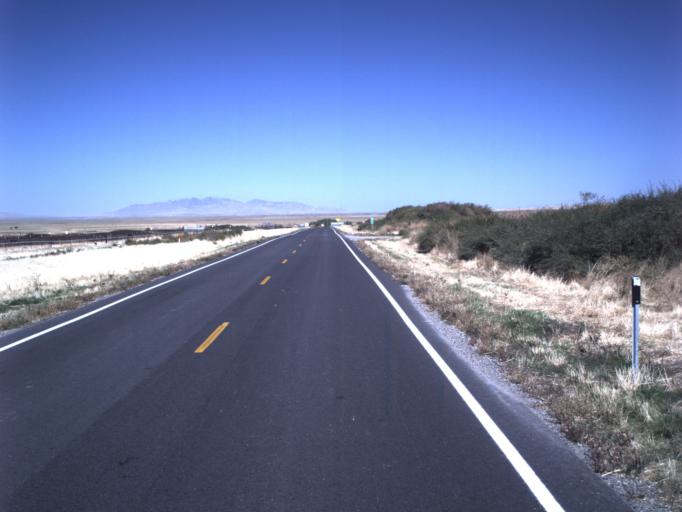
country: US
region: Utah
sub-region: Tooele County
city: Grantsville
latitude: 40.5281
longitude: -112.7477
